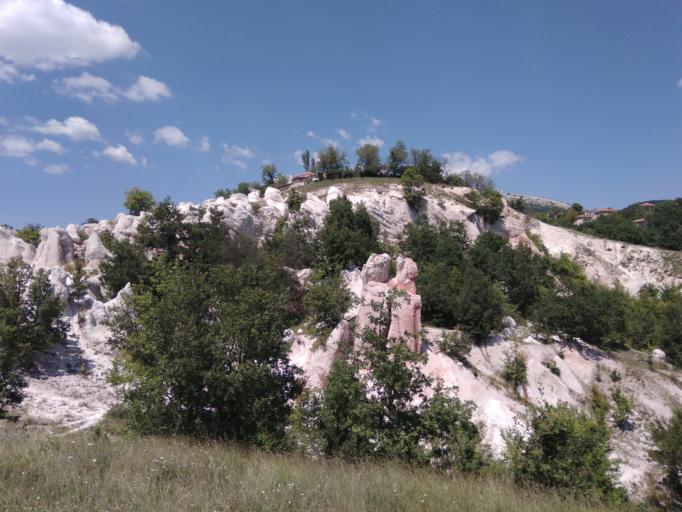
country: BG
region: Kurdzhali
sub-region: Obshtina Kurdzhali
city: Kurdzhali
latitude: 41.6563
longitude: 25.3995
